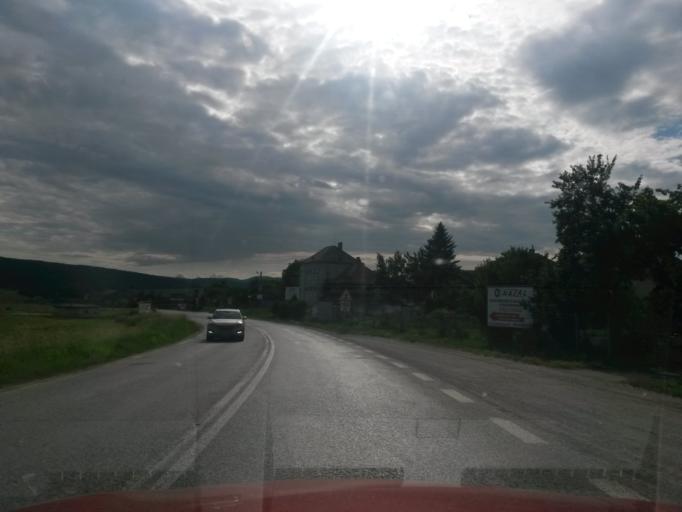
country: SK
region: Presovsky
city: Sabinov
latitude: 49.0096
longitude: 21.1291
